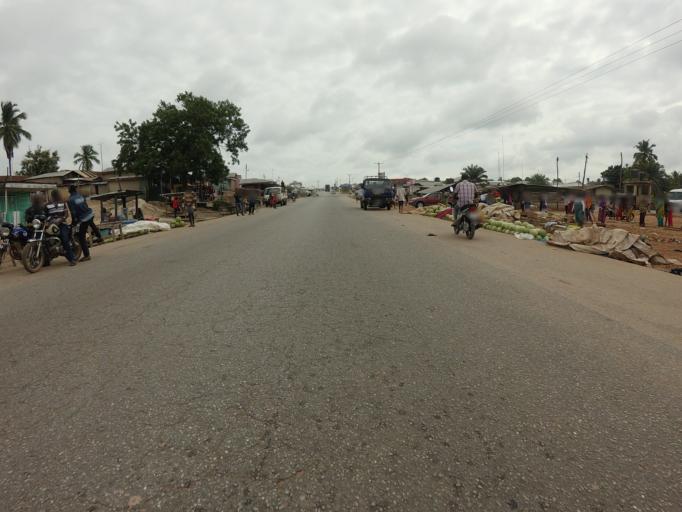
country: GH
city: Bechem
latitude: 7.1313
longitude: -1.7346
